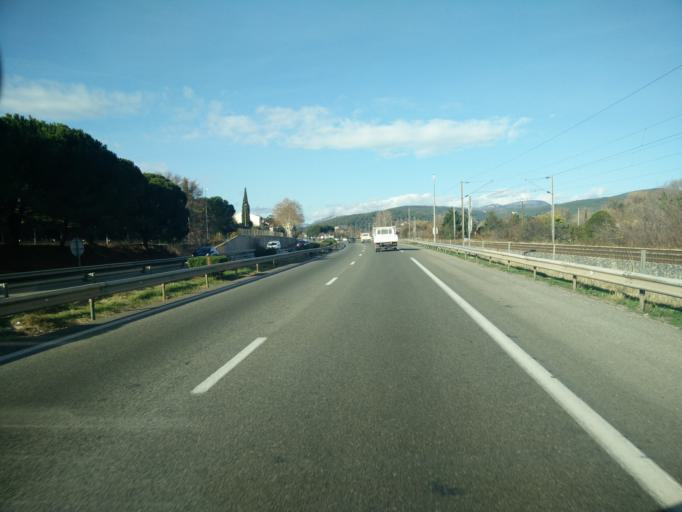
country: FR
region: Provence-Alpes-Cote d'Azur
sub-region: Departement du Var
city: La Farlede
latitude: 43.1770
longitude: 6.0481
